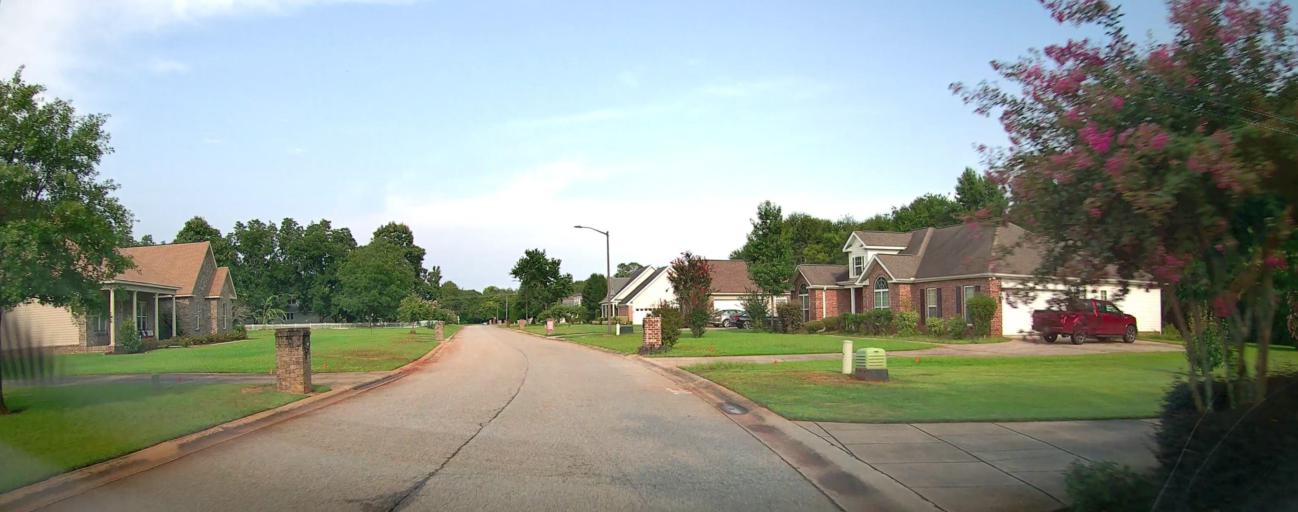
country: US
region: Georgia
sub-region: Houston County
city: Centerville
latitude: 32.6376
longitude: -83.7122
